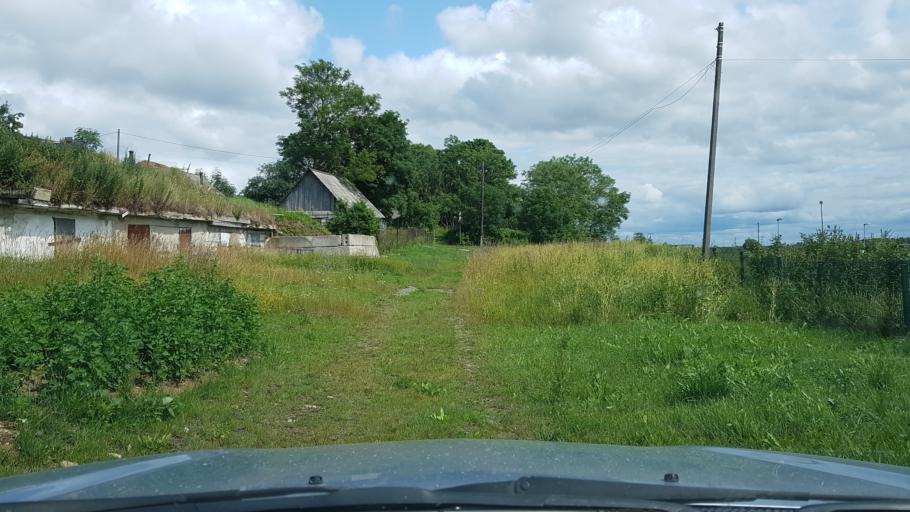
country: EE
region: Ida-Virumaa
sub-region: Sillamaee linn
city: Sillamae
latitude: 59.3722
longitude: 27.8719
